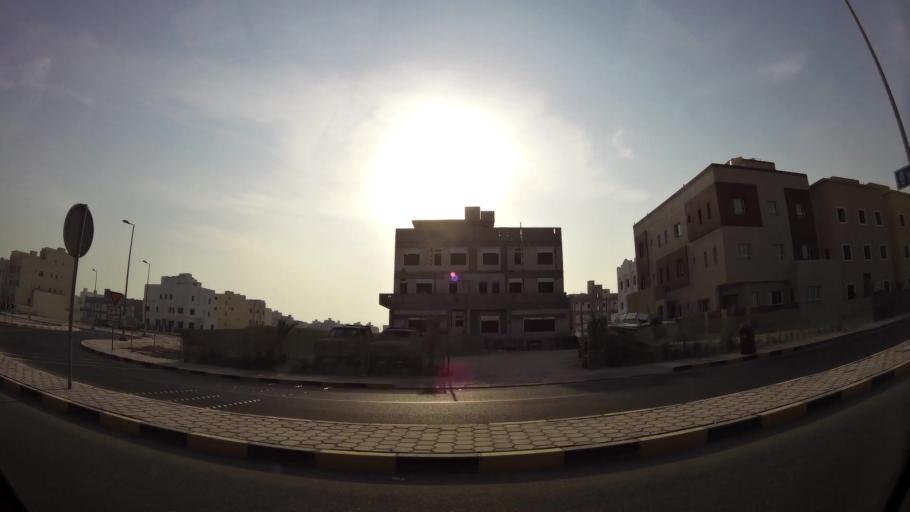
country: KW
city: Al Funaytis
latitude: 29.2263
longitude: 48.0911
